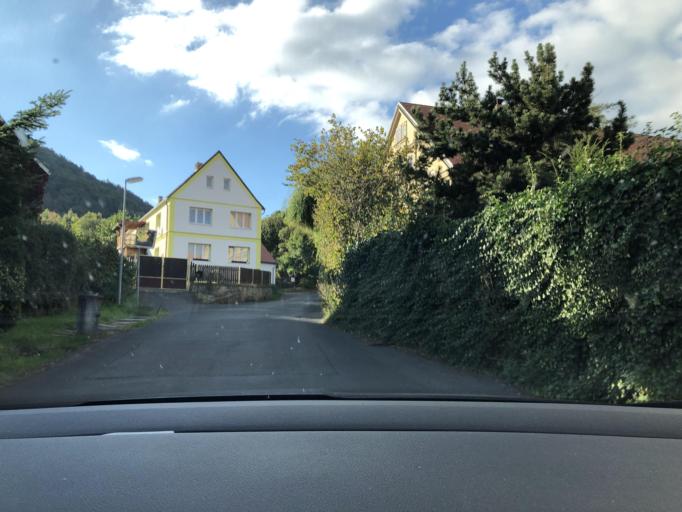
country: CZ
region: Ustecky
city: Zitenice
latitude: 50.5896
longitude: 14.1664
